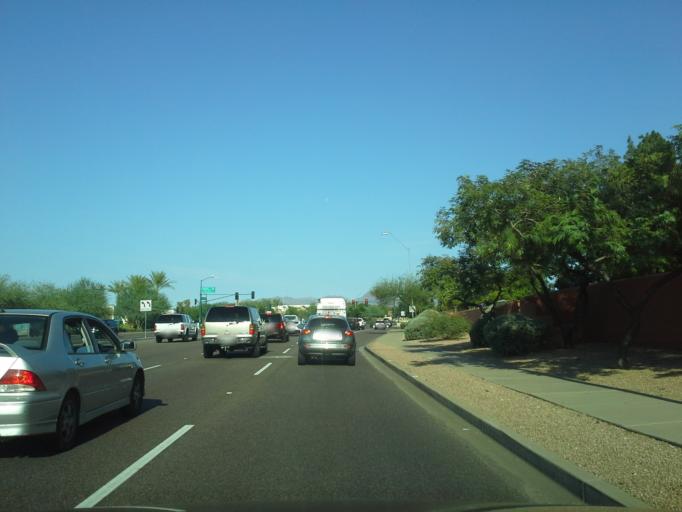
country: US
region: Arizona
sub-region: Maricopa County
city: Paradise Valley
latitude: 33.5989
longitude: -111.9891
